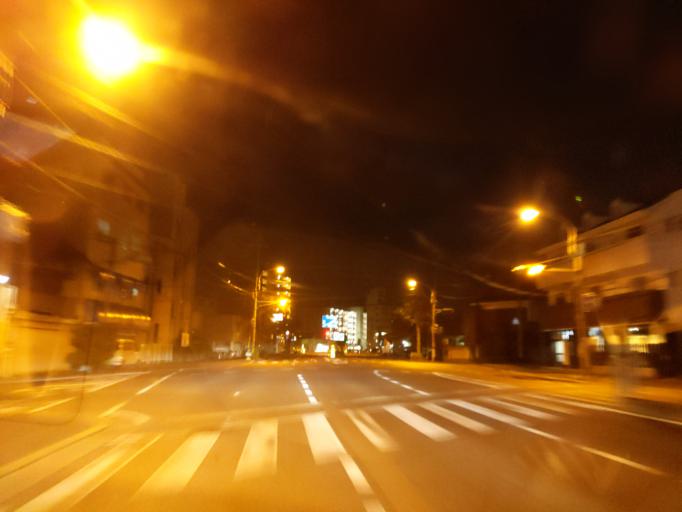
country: JP
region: Okayama
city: Okayama-shi
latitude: 34.6645
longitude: 133.9437
